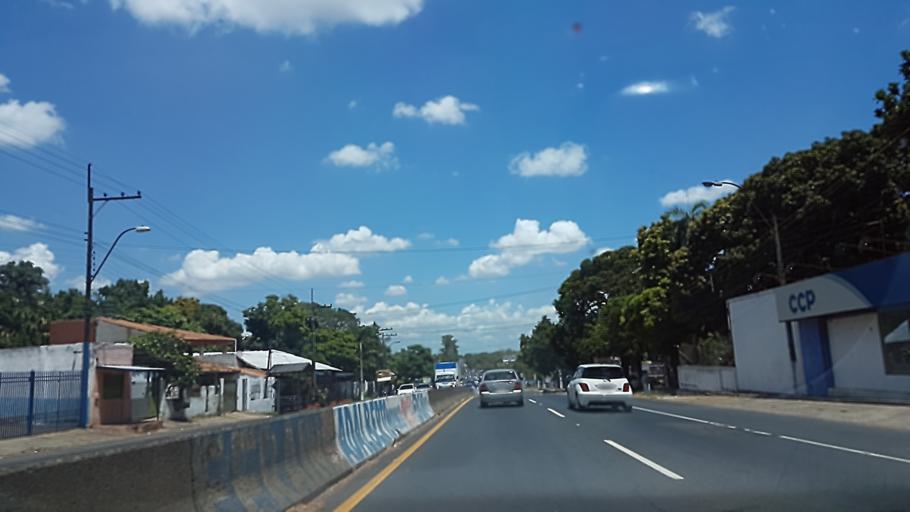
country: PY
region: Central
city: Capiata
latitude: -25.3464
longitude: -57.4755
